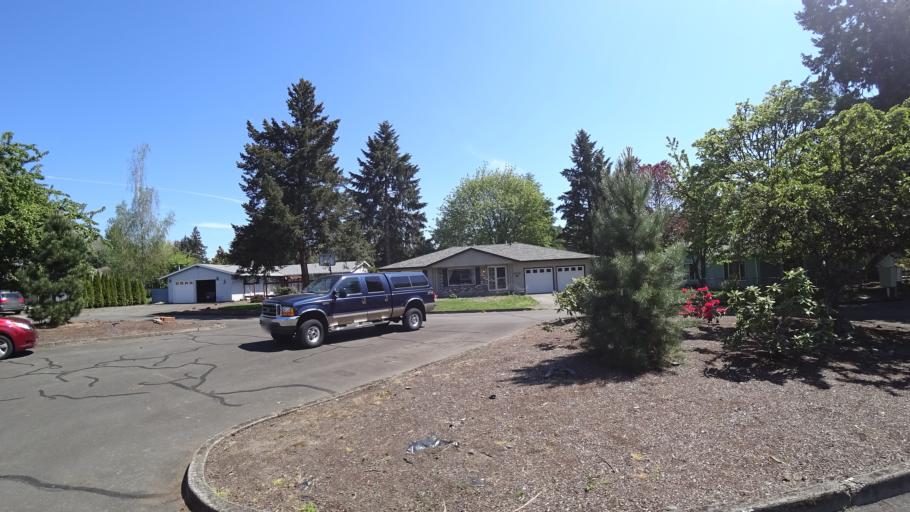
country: US
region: Oregon
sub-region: Washington County
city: Hillsboro
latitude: 45.4996
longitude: -122.9553
